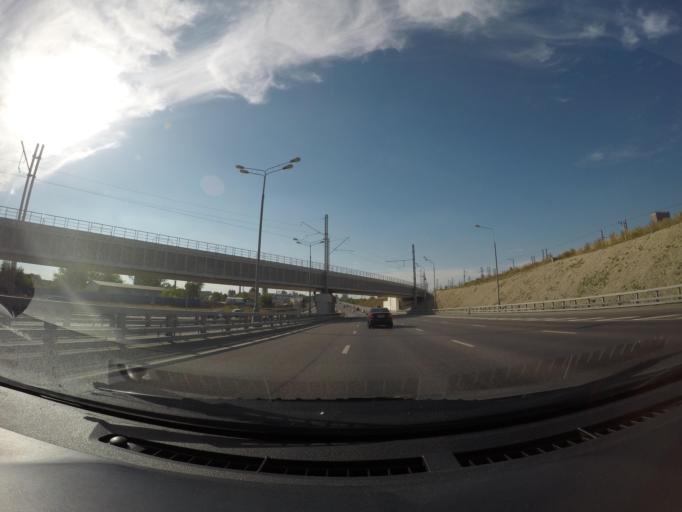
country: RU
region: Moscow
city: Zapadnoye Degunino
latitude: 55.8541
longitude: 37.5448
